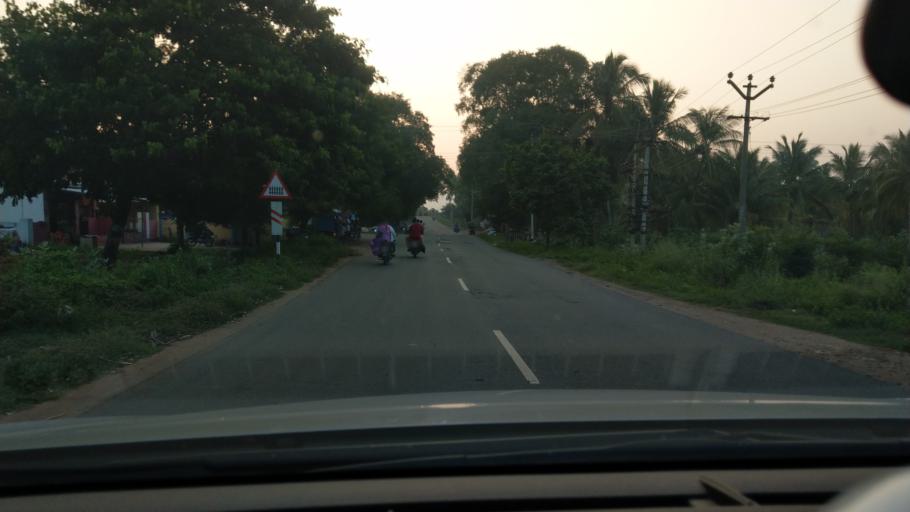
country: IN
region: Tamil Nadu
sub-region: Salem
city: Attur
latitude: 11.5991
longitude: 78.5776
